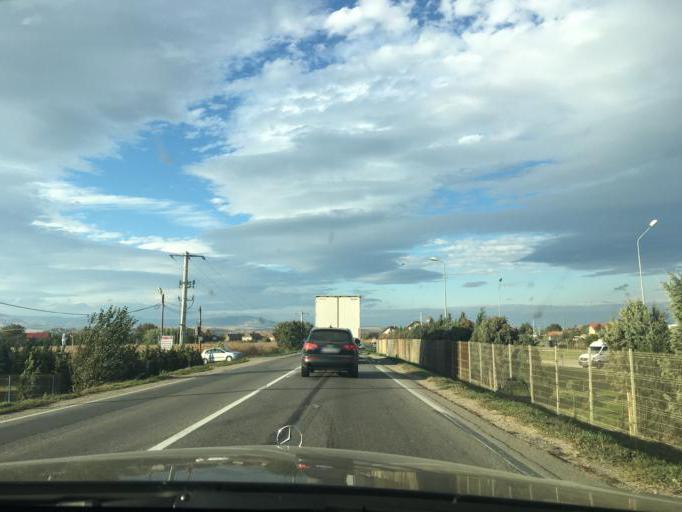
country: RO
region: Alba
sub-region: Comuna Santimbru
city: Santimbru
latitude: 46.1552
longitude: 23.6429
